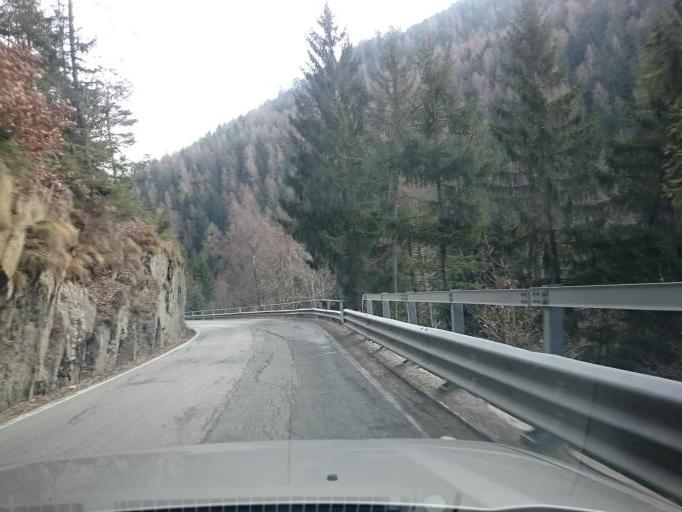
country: IT
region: Lombardy
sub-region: Provincia di Brescia
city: Corteno Golgi
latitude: 46.1626
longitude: 10.1987
